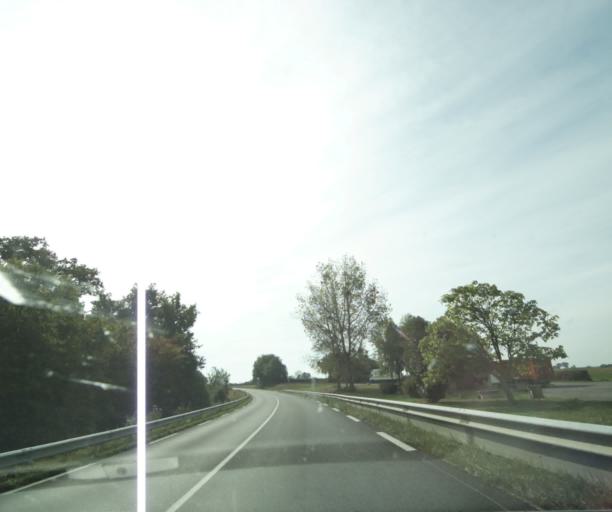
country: FR
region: Auvergne
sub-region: Departement de l'Allier
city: Saint-Francois
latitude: 46.4345
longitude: 3.9072
